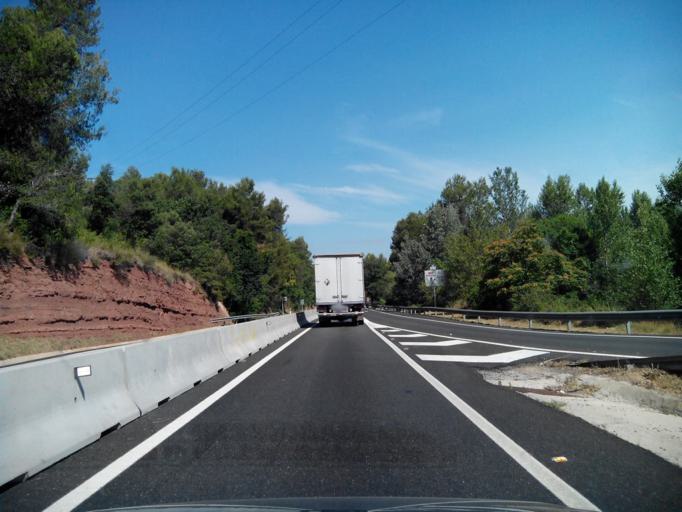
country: ES
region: Catalonia
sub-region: Provincia de Barcelona
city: Monistrol de Montserrat
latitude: 41.5976
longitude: 1.8944
